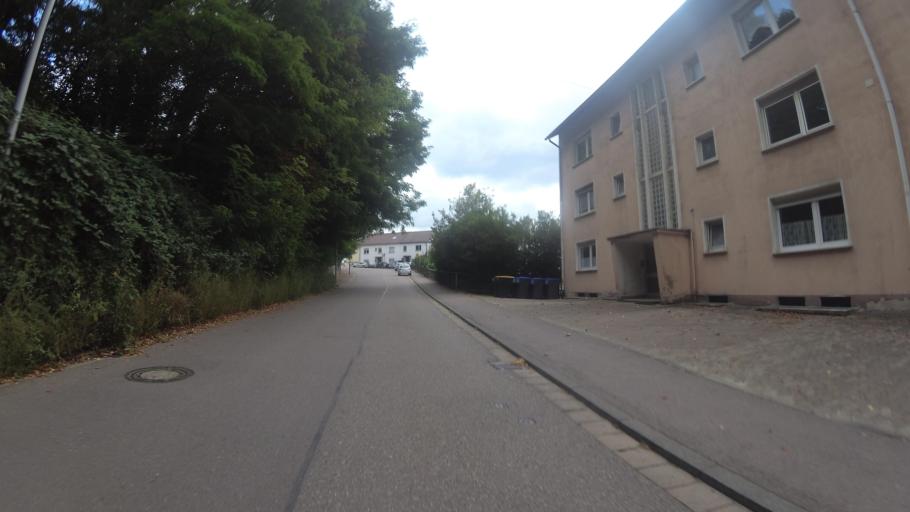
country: DE
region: Saarland
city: Puttlingen
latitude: 49.2612
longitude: 6.9066
